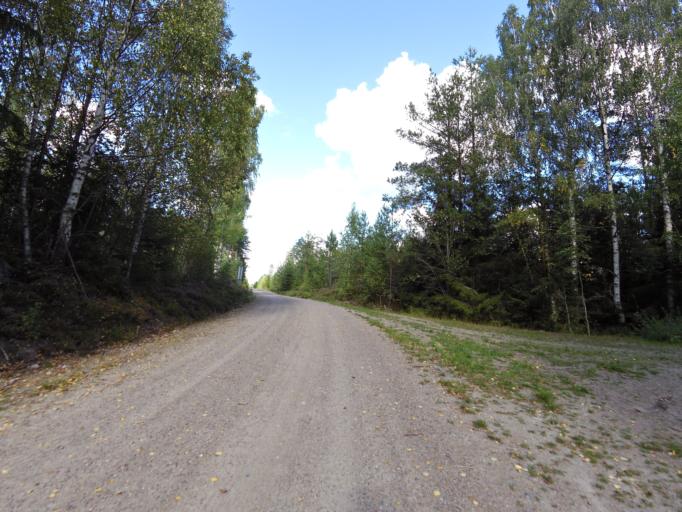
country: SE
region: Gaevleborg
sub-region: Ockelbo Kommun
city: Ockelbo
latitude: 60.8473
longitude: 16.8108
